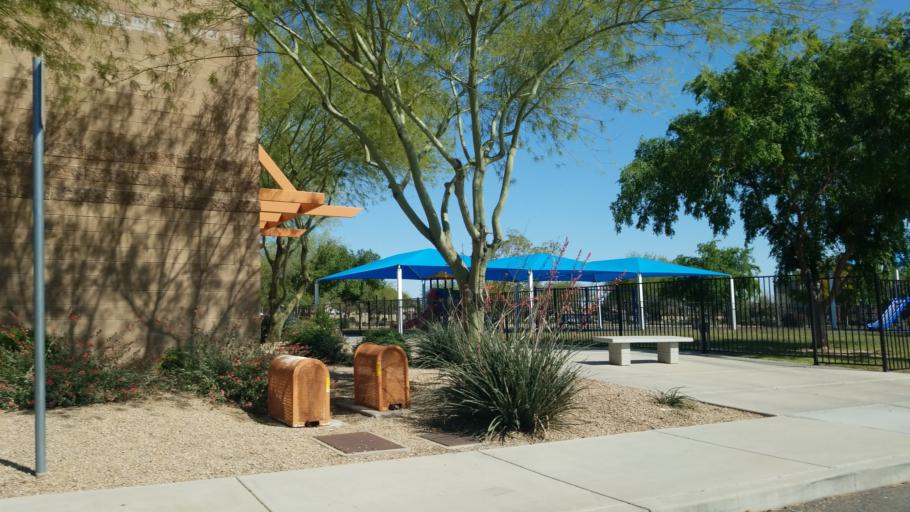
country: US
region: Arizona
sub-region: Maricopa County
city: Glendale
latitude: 33.5793
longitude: -112.1880
